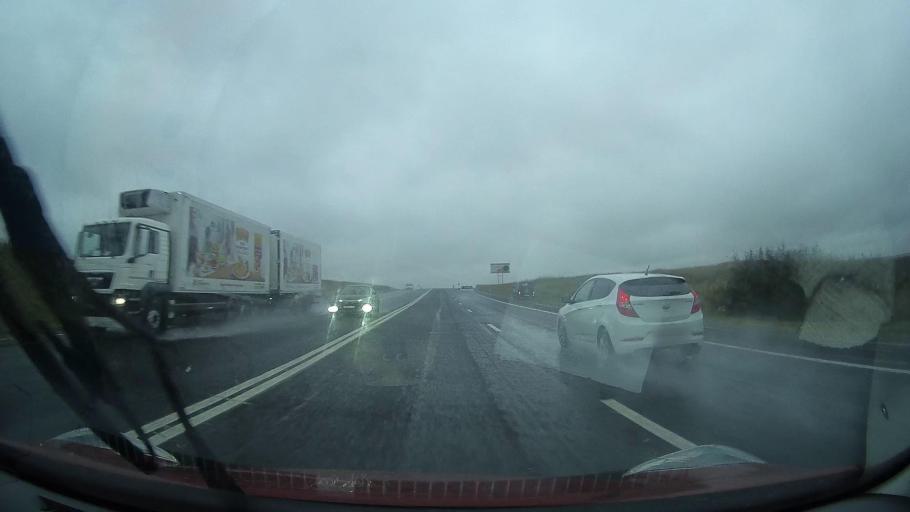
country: RU
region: Stavropol'skiy
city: Nevinnomyssk
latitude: 44.6238
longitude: 42.0686
